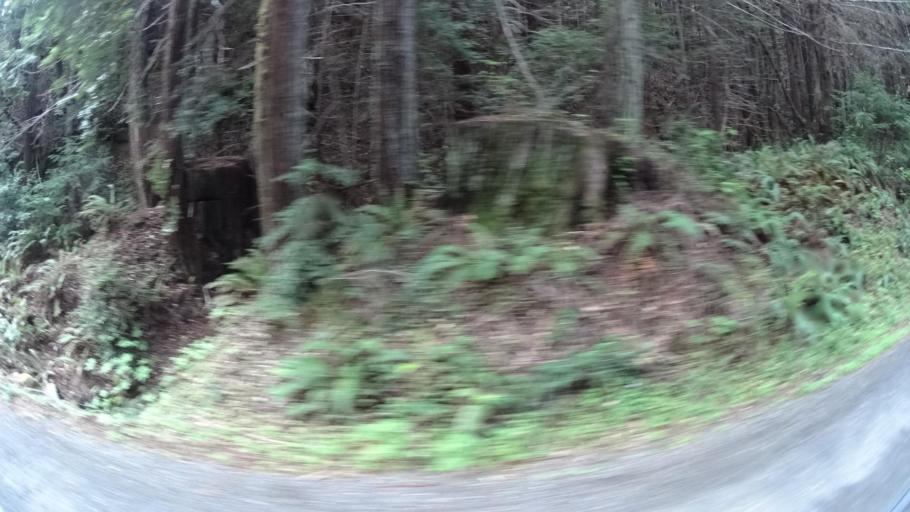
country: US
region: California
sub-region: Humboldt County
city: Redway
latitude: 40.3365
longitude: -123.8561
